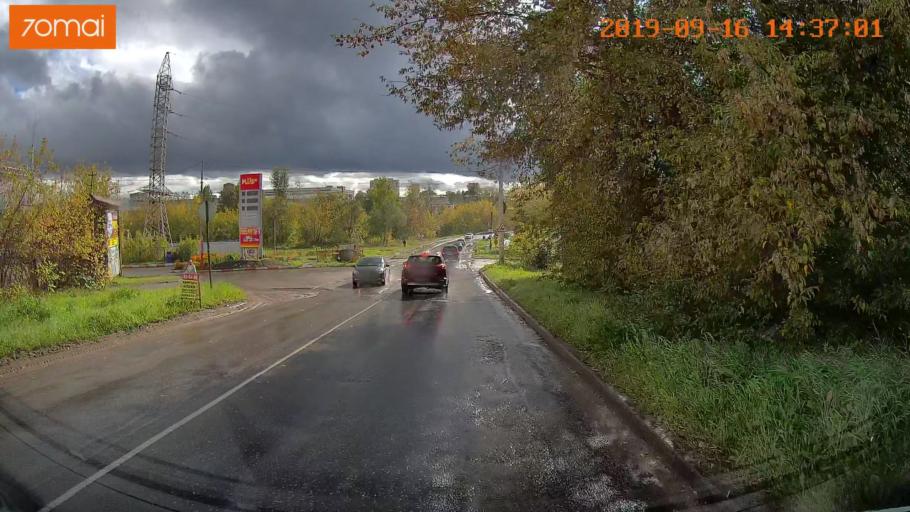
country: RU
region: Ivanovo
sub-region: Gorod Ivanovo
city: Ivanovo
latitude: 57.0151
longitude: 40.9557
